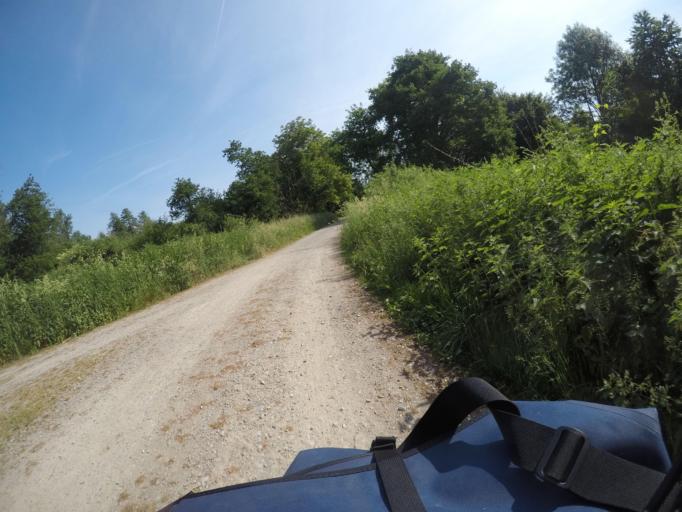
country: DE
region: Baden-Wuerttemberg
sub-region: Karlsruhe Region
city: Bietigheim
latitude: 48.9116
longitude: 8.2376
